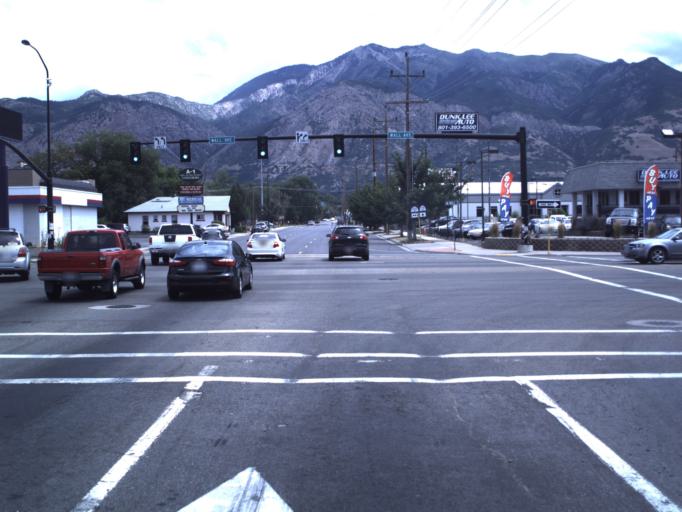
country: US
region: Utah
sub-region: Weber County
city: Ogden
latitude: 41.2082
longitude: -111.9797
